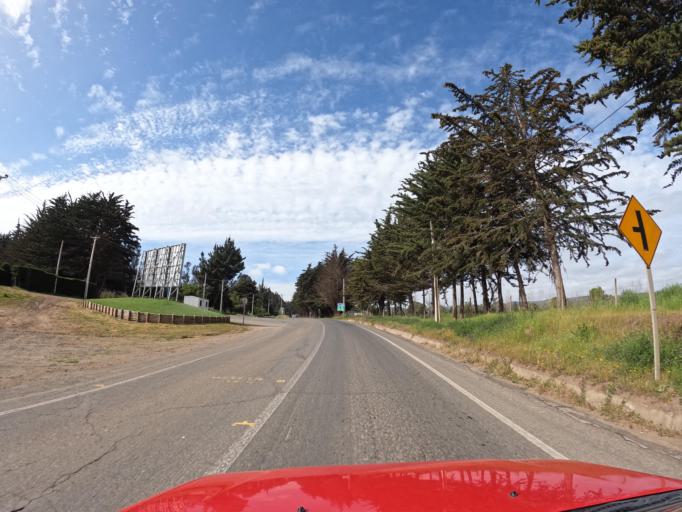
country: CL
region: O'Higgins
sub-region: Provincia de Colchagua
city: Santa Cruz
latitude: -34.3817
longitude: -71.9741
